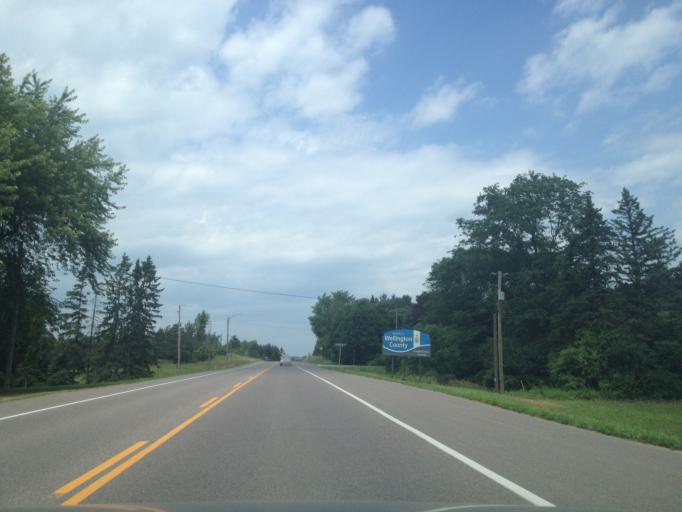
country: CA
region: Ontario
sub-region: Wellington County
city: Guelph
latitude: 43.5794
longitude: -80.2462
